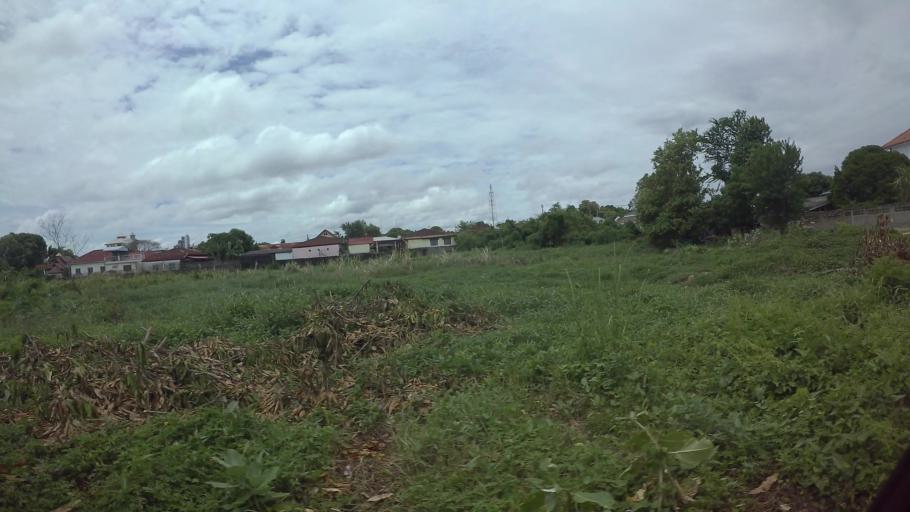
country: TH
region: Chon Buri
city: Sattahip
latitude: 12.7582
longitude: 100.8975
